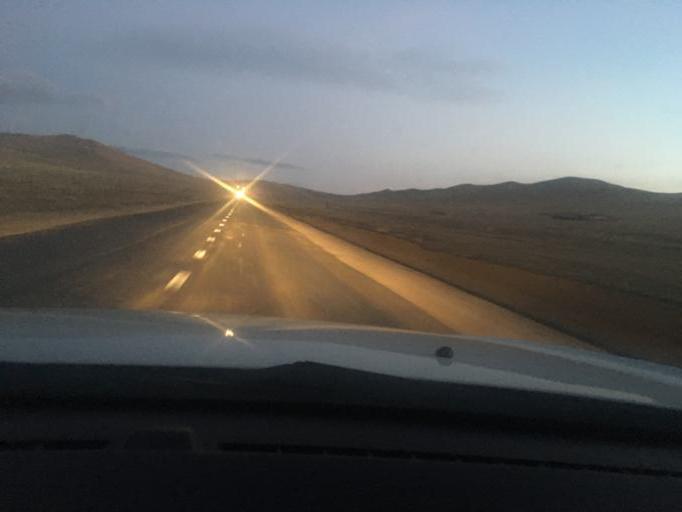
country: MN
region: Ulaanbaatar
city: Ulaanbaatar
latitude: 47.9842
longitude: 106.5663
